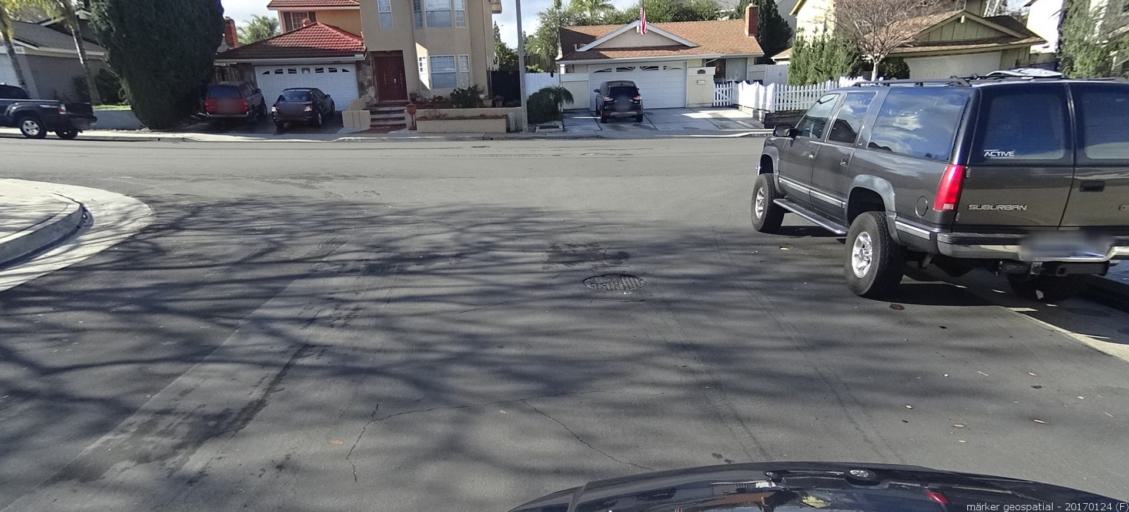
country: US
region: California
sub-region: Orange County
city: Laguna Hills
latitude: 33.6270
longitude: -117.7097
